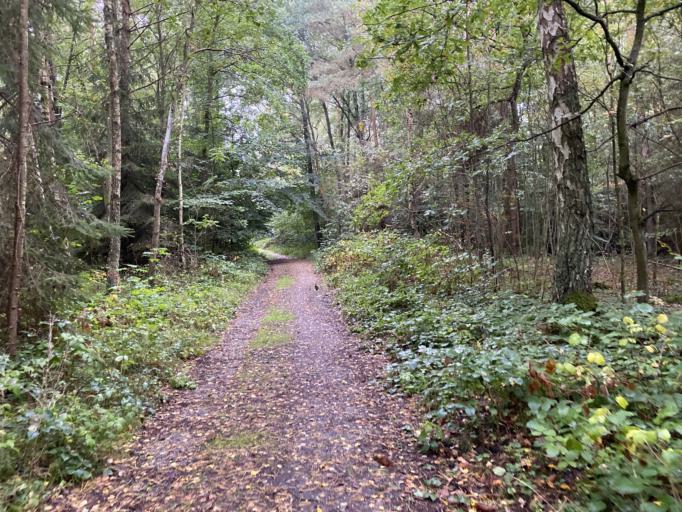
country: DE
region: Mecklenburg-Vorpommern
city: Ostseebad Binz
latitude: 54.4473
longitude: 13.5572
